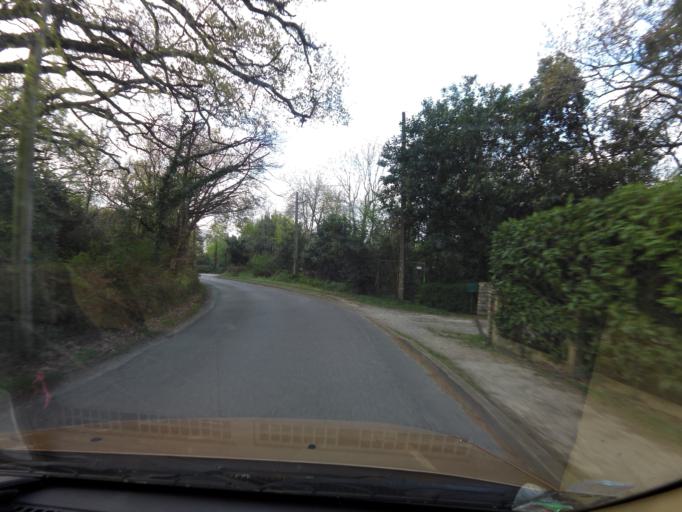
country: FR
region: Brittany
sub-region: Departement du Morbihan
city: Arradon
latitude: 47.6283
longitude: -2.8159
